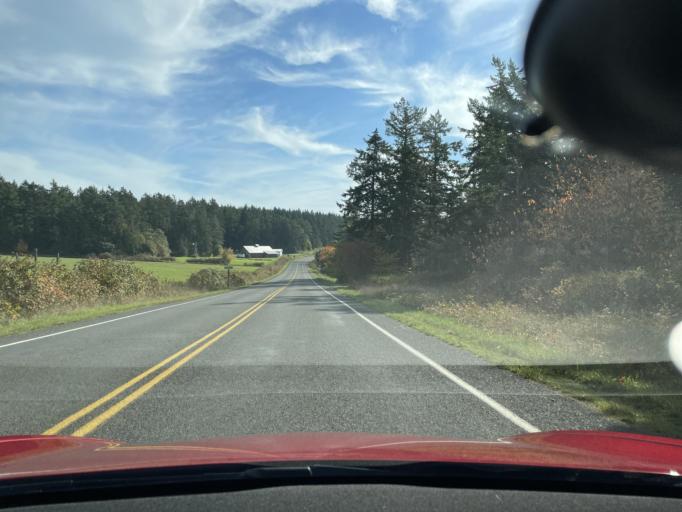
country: US
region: Washington
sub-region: San Juan County
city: Friday Harbor
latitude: 48.6097
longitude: -123.1406
